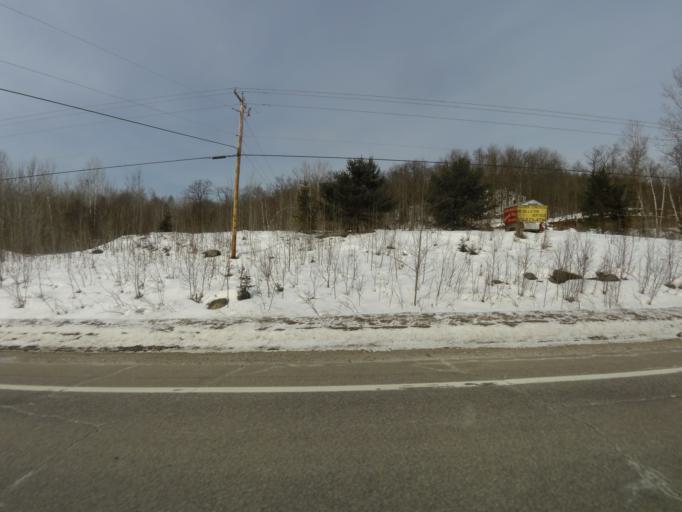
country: CA
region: Quebec
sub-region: Laurentides
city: Mont-Laurier
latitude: 46.3215
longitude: -75.5512
